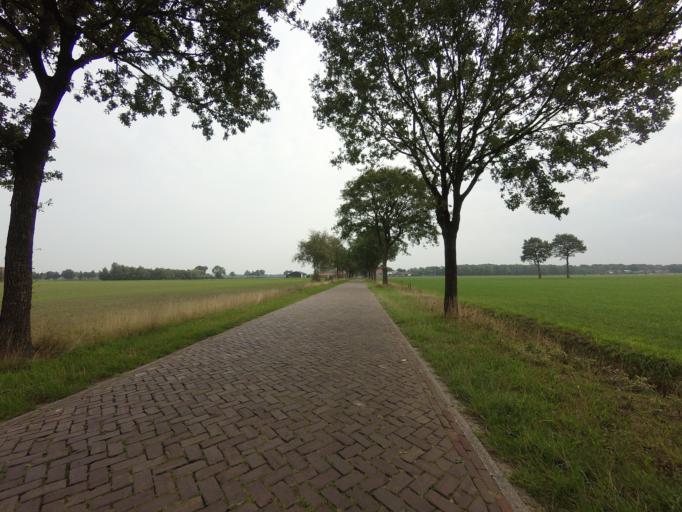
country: NL
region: Drenthe
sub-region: Gemeente Westerveld
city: Dwingeloo
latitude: 52.8691
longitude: 6.4370
